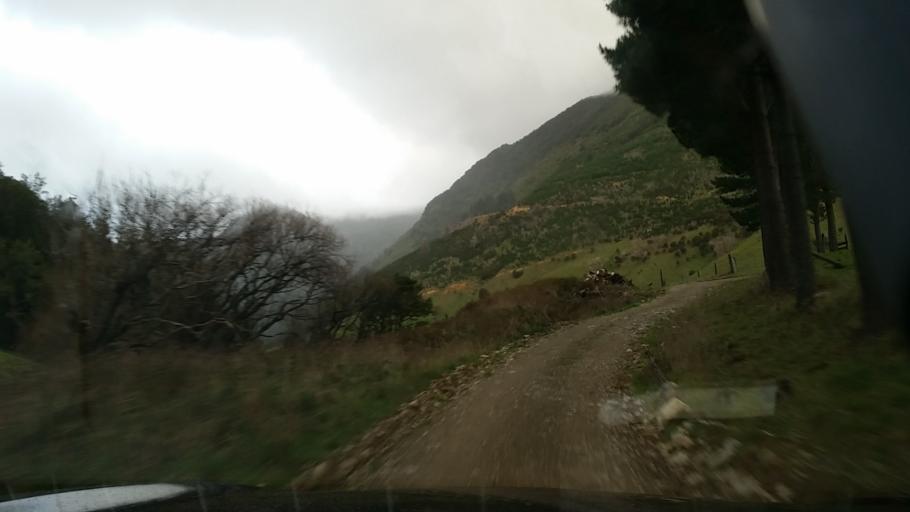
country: NZ
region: Marlborough
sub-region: Marlborough District
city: Picton
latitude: -41.2158
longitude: 173.6984
